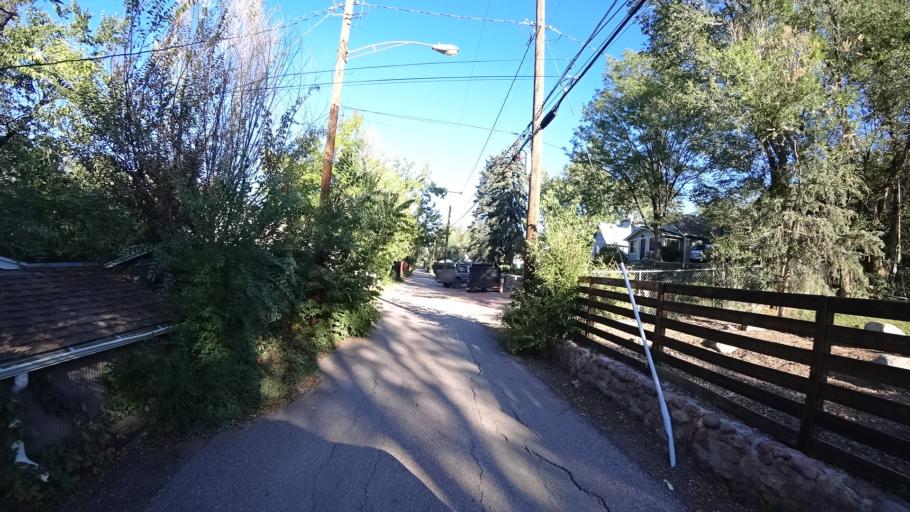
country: US
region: Colorado
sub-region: El Paso County
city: Colorado Springs
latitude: 38.8387
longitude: -104.8423
